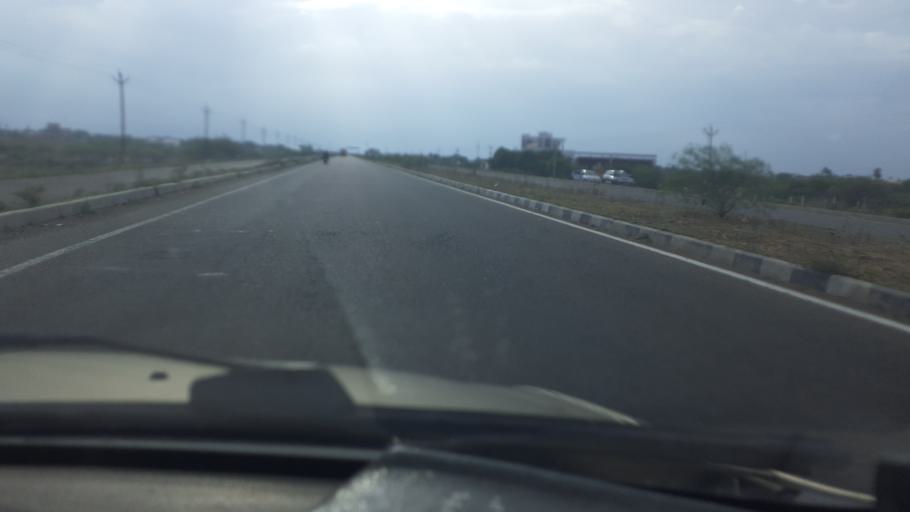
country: IN
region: Tamil Nadu
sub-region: Tirunelveli Kattabo
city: Tirunelveli
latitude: 8.6637
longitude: 77.7292
